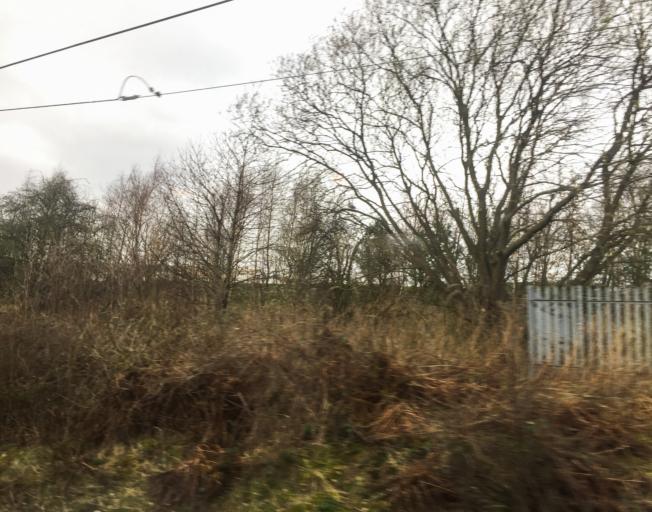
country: GB
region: Scotland
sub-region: West Dunbartonshire
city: Clydebank
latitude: 55.9050
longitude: -4.3834
